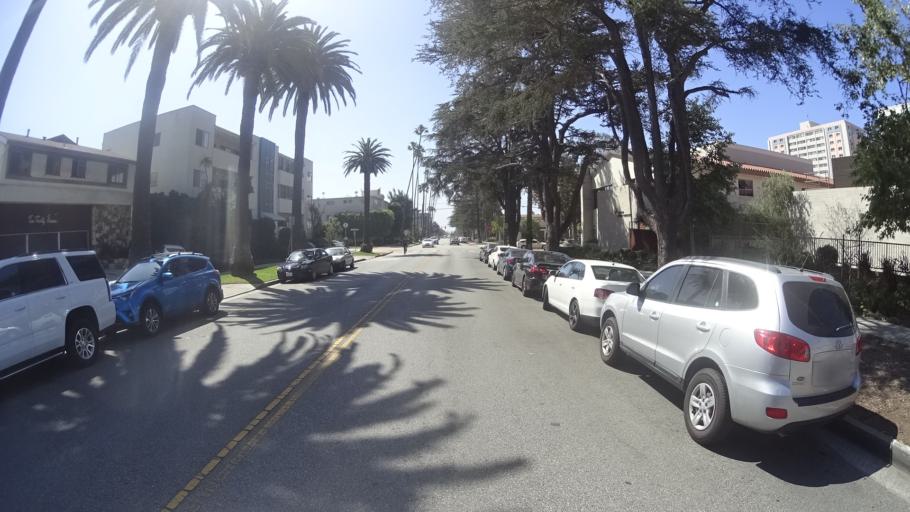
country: US
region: California
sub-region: Los Angeles County
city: Santa Monica
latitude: 34.0241
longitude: -118.4967
